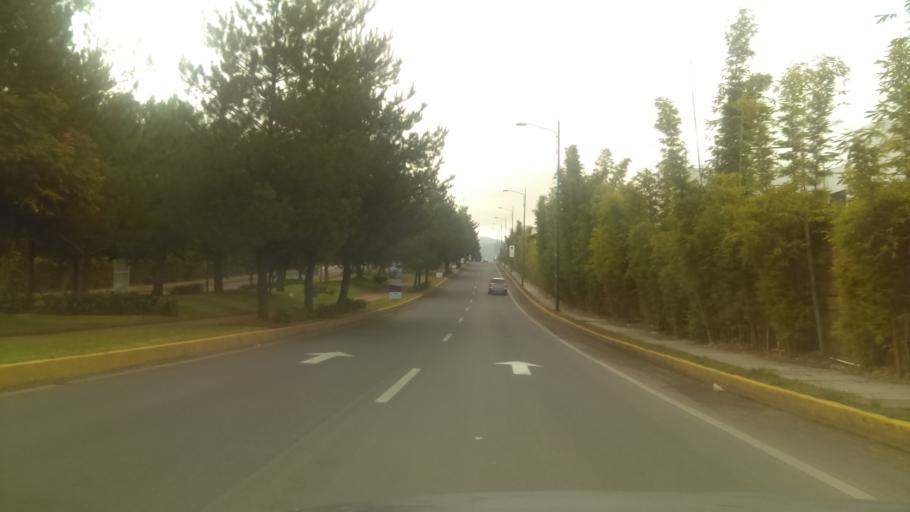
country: MX
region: Michoacan
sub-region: Morelia
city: Montana Monarca (Punta Altozano)
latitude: 19.6634
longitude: -101.1646
